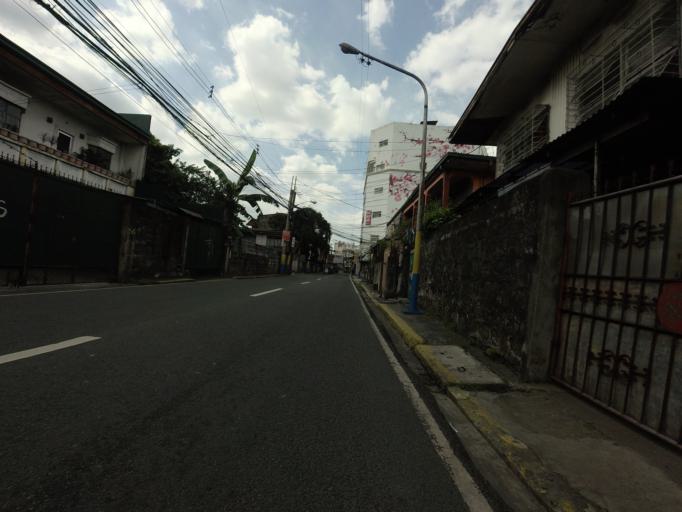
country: PH
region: Metro Manila
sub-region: Mandaluyong
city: Mandaluyong City
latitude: 14.5889
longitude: 121.0313
